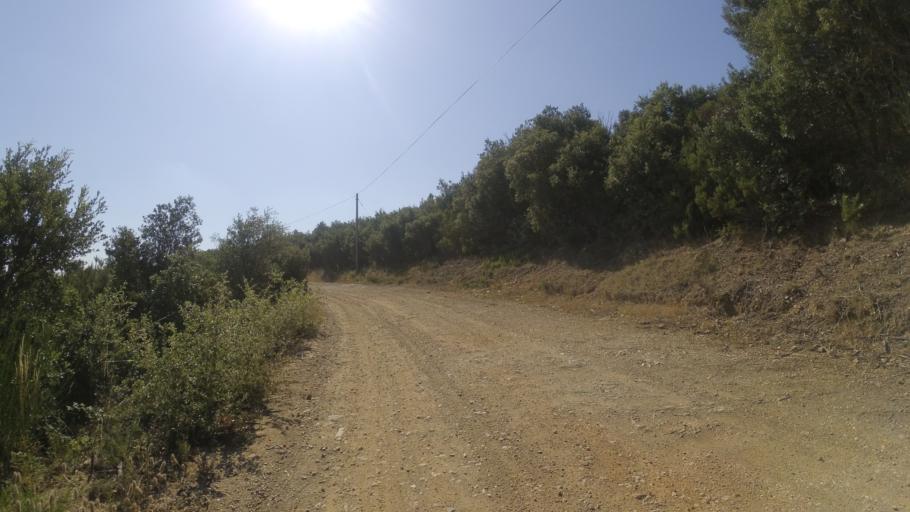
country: FR
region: Languedoc-Roussillon
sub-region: Departement des Pyrenees-Orientales
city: Thuir
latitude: 42.6158
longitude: 2.6789
